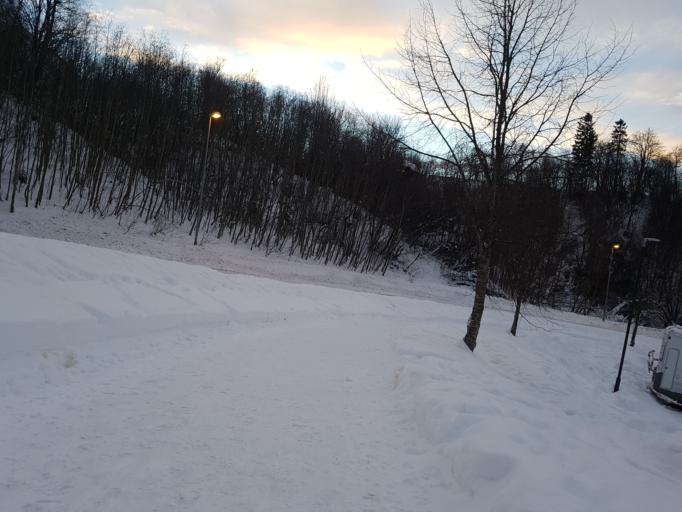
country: NO
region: Sor-Trondelag
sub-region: Trondheim
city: Trondheim
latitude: 63.3784
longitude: 10.3833
